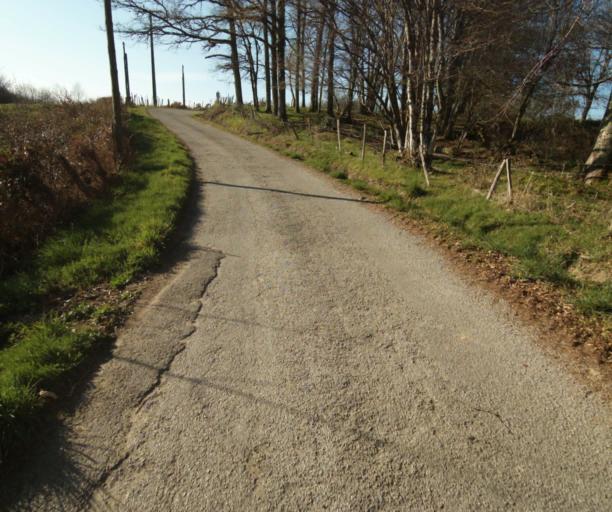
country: FR
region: Limousin
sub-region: Departement de la Correze
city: Chamboulive
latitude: 45.4931
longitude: 1.7267
